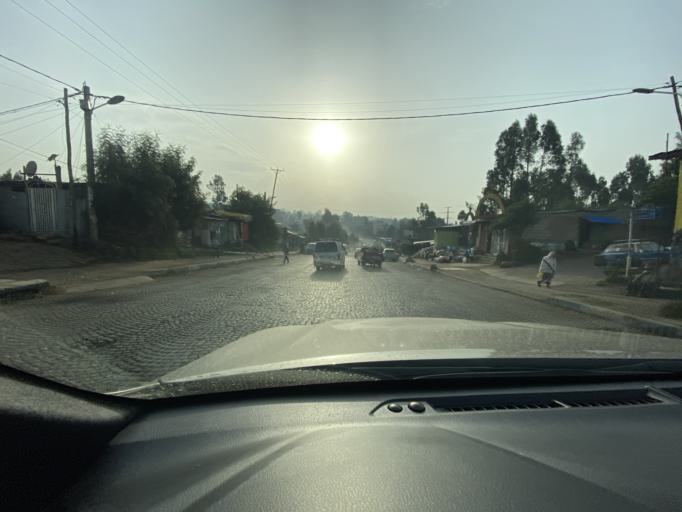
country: ET
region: Adis Abeba
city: Addis Ababa
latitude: 9.0213
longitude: 38.7172
